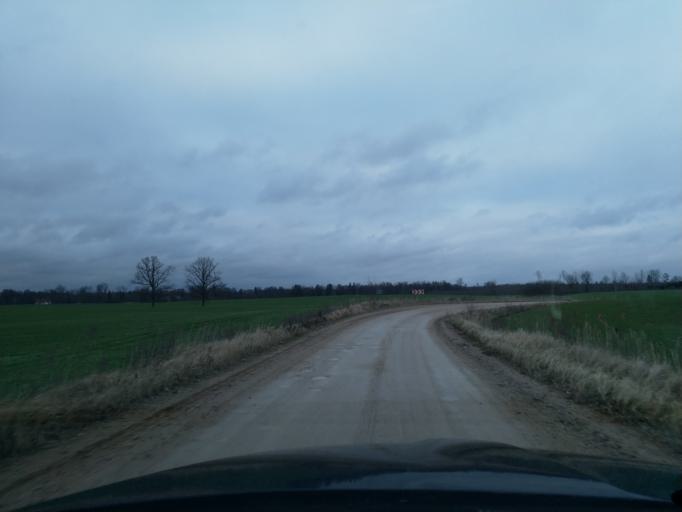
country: LV
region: Saldus Rajons
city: Saldus
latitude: 56.8945
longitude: 22.2962
